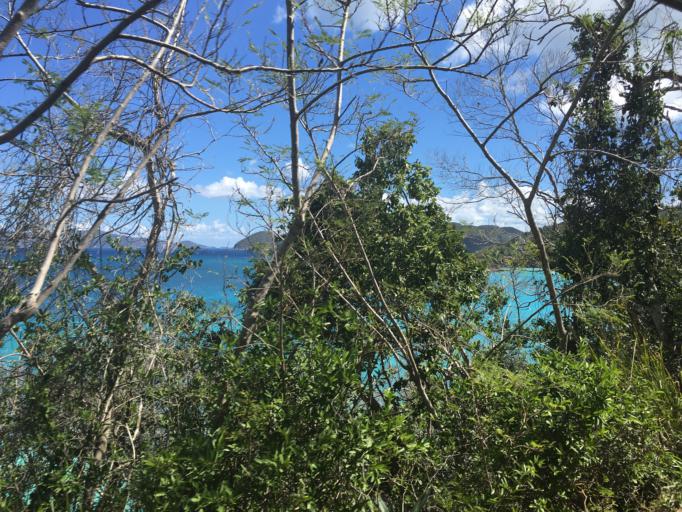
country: VI
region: Saint John Island
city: Cruz Bay
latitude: 18.3514
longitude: -64.7730
